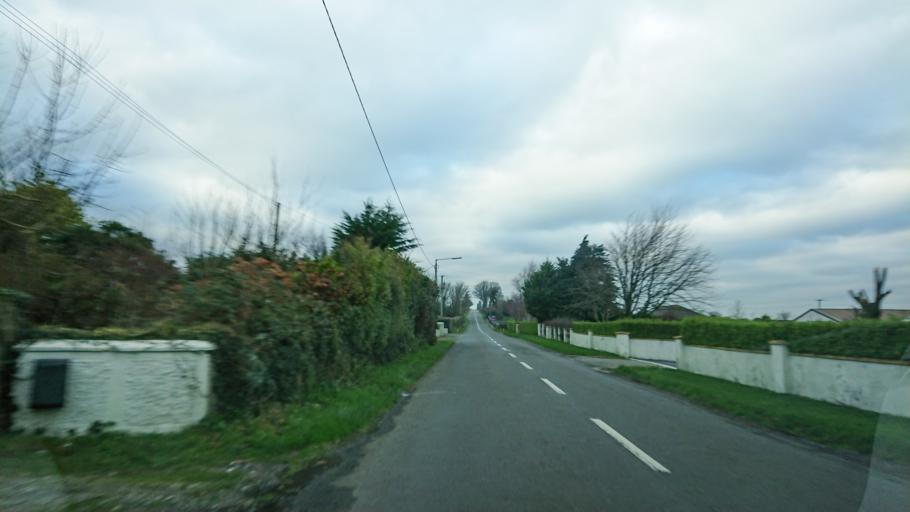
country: IE
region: Munster
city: Carrick-on-Suir
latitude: 52.3107
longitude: -7.5167
